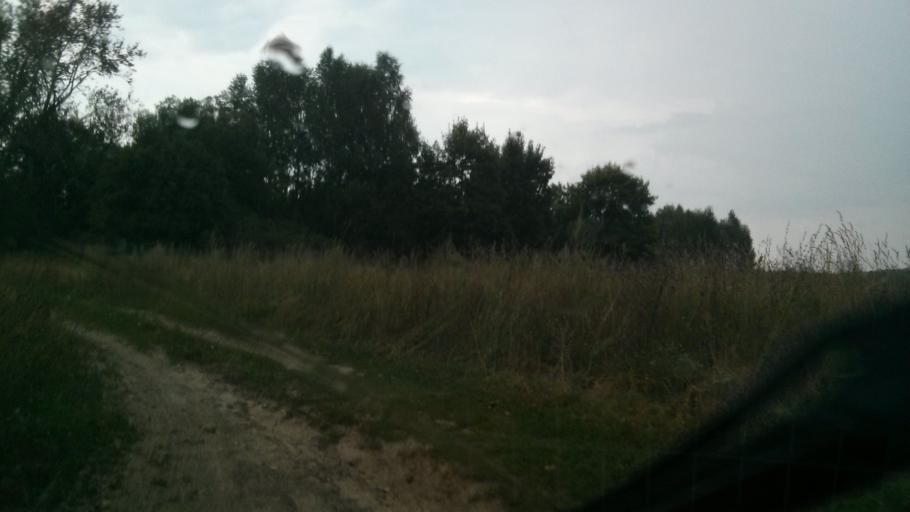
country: RU
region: Nizjnij Novgorod
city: Shimorskoye
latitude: 55.3088
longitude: 41.8654
